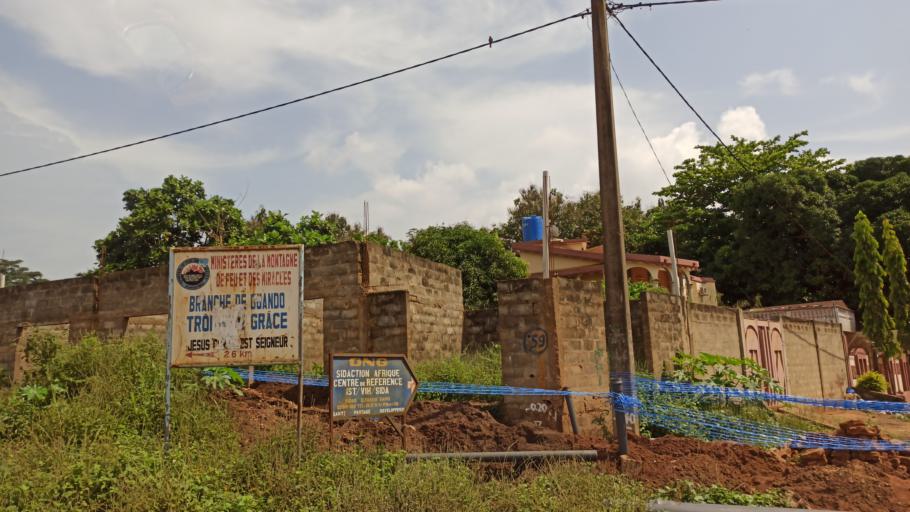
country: BJ
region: Queme
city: Porto-Novo
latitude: 6.4776
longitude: 2.5940
